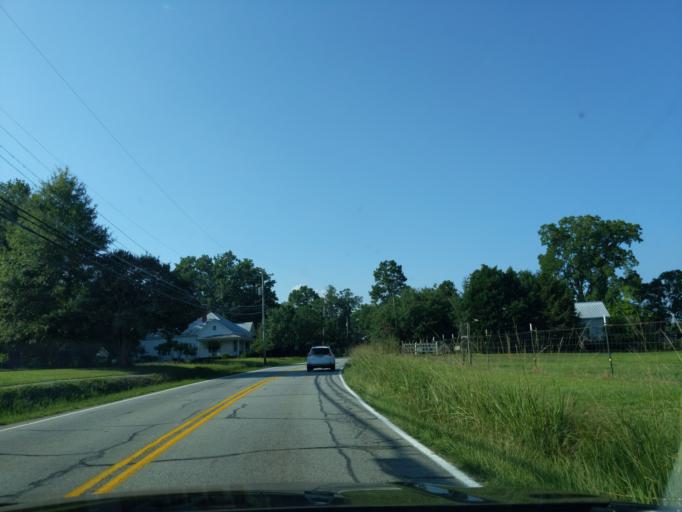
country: US
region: South Carolina
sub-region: Newberry County
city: Prosperity
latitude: 34.2016
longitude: -81.5300
